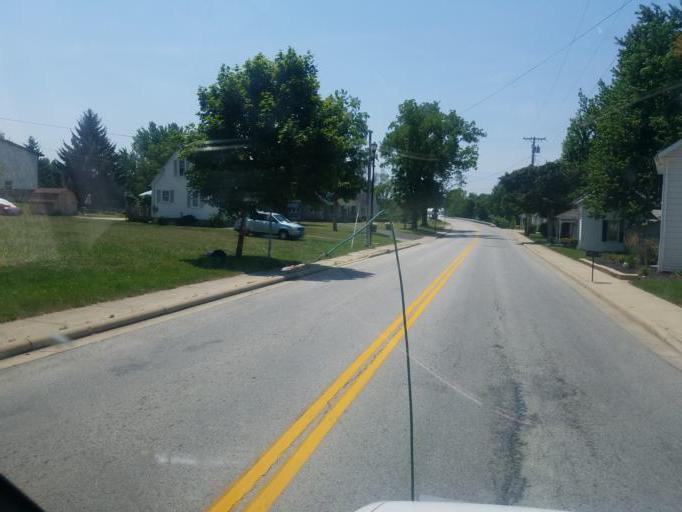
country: US
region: Ohio
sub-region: Shelby County
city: Fort Loramie
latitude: 40.3501
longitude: -84.3763
